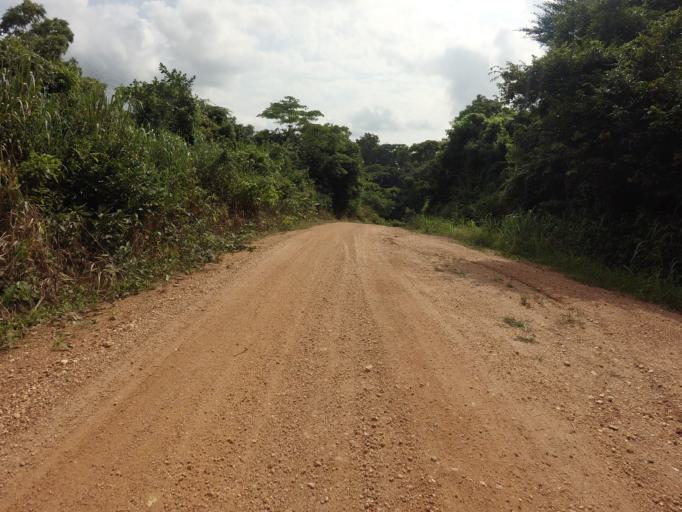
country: GH
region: Volta
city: Kpandu
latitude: 6.8742
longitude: 0.4286
